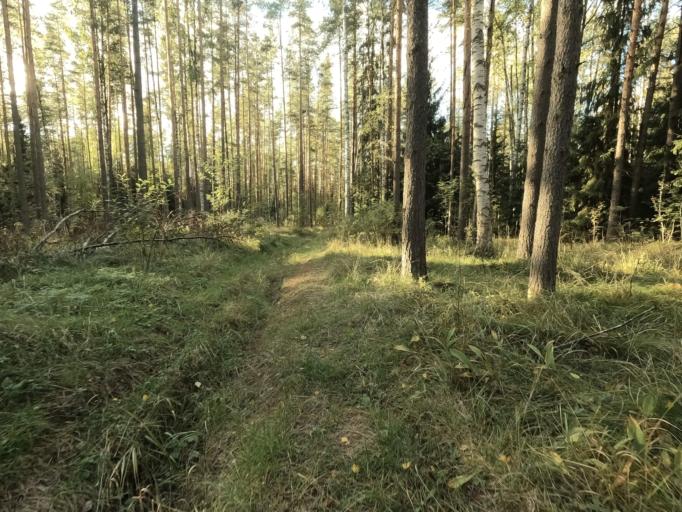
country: RU
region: Leningrad
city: Imeni Sverdlova
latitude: 59.8465
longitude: 30.7295
